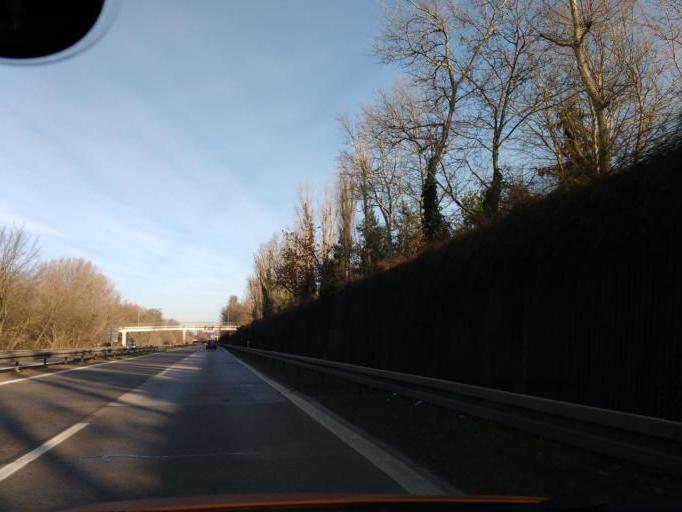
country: DE
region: Berlin
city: Blankenburg
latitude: 52.5991
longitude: 13.4463
